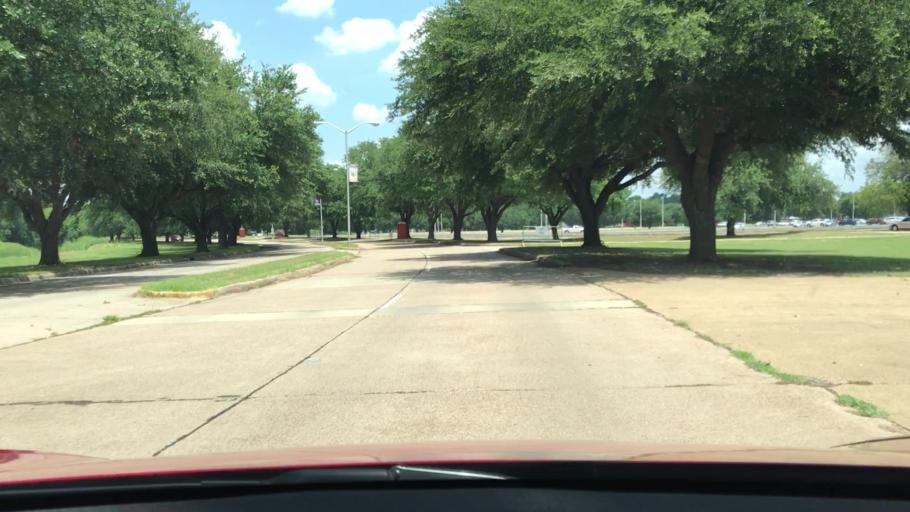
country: US
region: Louisiana
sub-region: Bossier Parish
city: Bossier City
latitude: 32.4293
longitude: -93.7077
